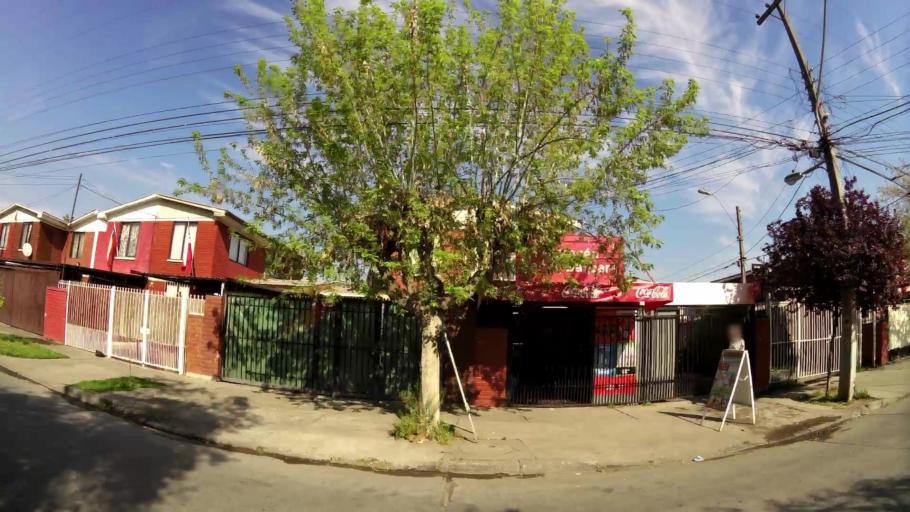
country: CL
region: Santiago Metropolitan
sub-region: Provincia de Santiago
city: La Pintana
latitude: -33.5567
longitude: -70.5998
